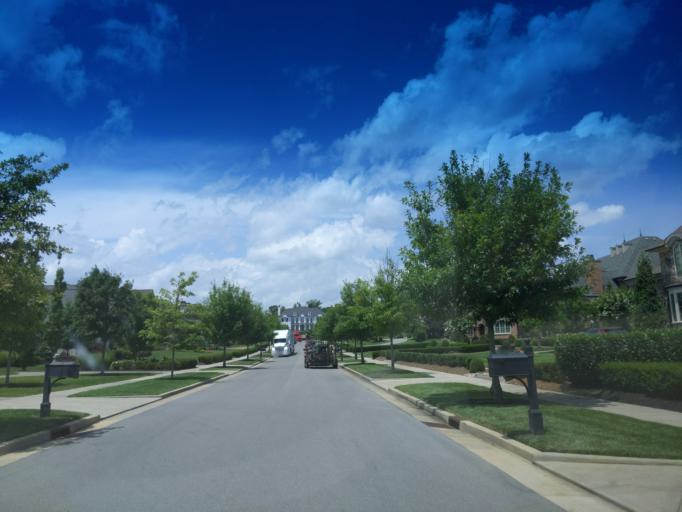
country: US
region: Tennessee
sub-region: Williamson County
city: Brentwood Estates
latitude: 36.0214
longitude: -86.7671
